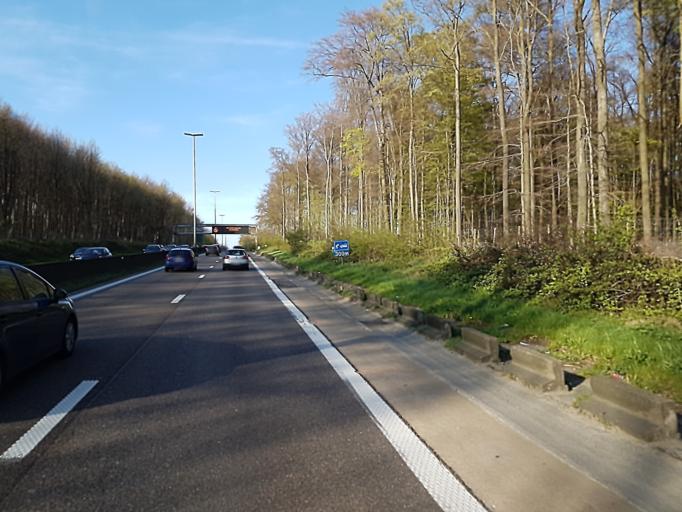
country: BE
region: Flanders
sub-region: Provincie Vlaams-Brabant
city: Hoeilaart
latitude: 50.7753
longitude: 4.4482
